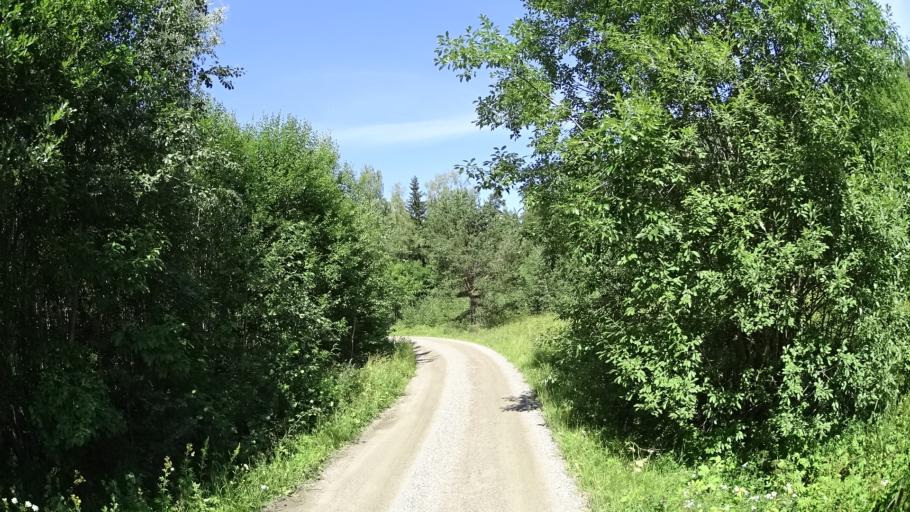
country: FI
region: Haeme
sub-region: Forssa
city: Tammela
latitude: 60.7685
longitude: 23.8711
